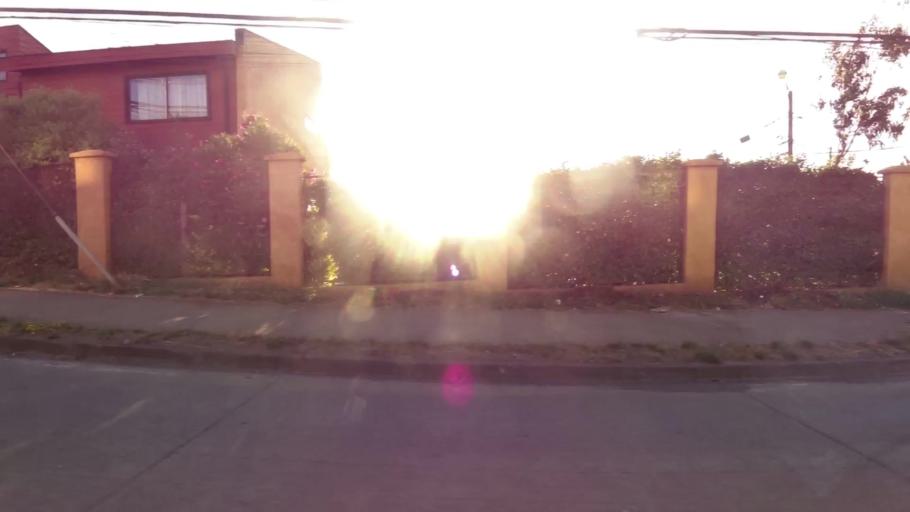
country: CL
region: Biobio
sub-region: Provincia de Concepcion
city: Concepcion
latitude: -36.8539
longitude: -73.0927
